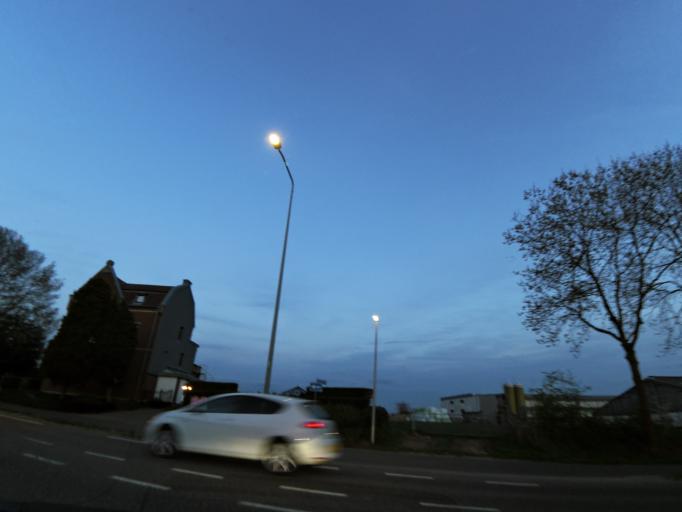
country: NL
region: Limburg
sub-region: Gemeente Simpelveld
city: Simpelveld
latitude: 50.8437
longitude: 5.9995
